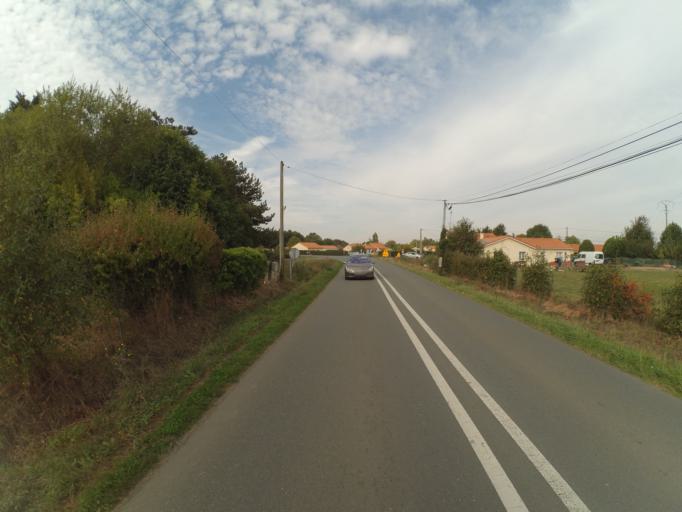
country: FR
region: Pays de la Loire
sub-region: Departement de Maine-et-Loire
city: Chemille-Melay
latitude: 47.2114
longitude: -0.7072
